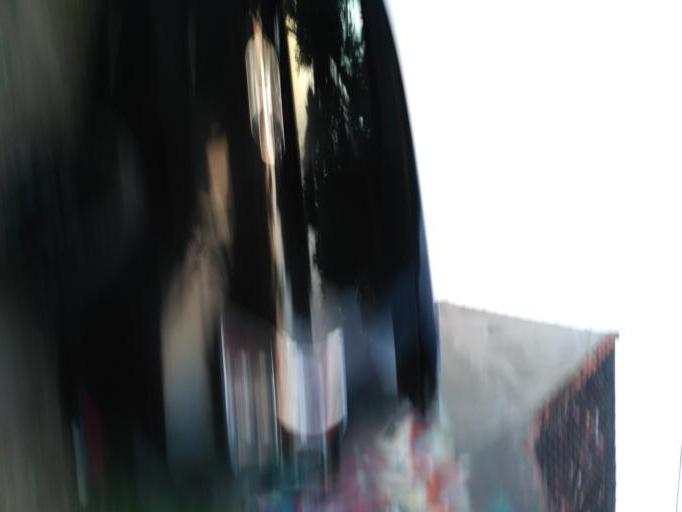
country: ID
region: Daerah Istimewa Yogyakarta
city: Sewon
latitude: -7.8970
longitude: 110.3701
